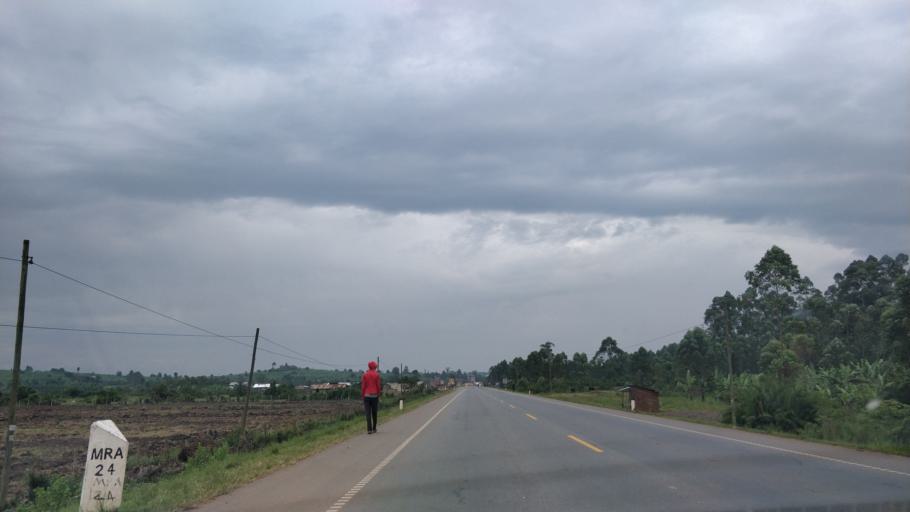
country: UG
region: Western Region
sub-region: Sheema District
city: Kibingo
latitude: -0.6654
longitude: 30.4485
